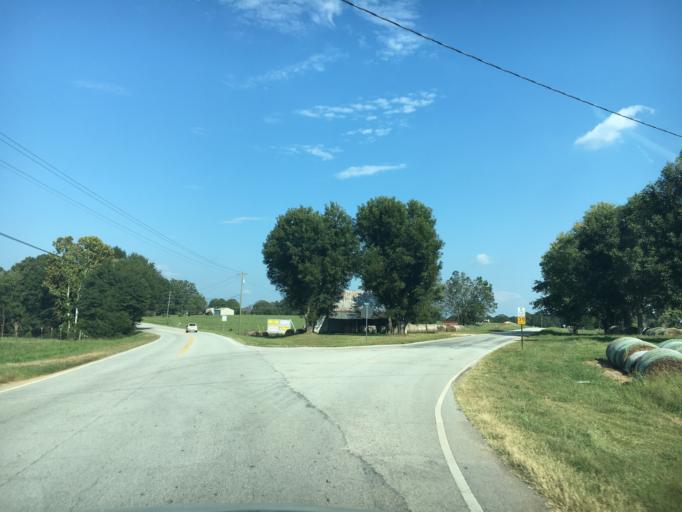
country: US
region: Georgia
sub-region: Franklin County
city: Gumlog
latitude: 34.4627
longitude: -83.0684
